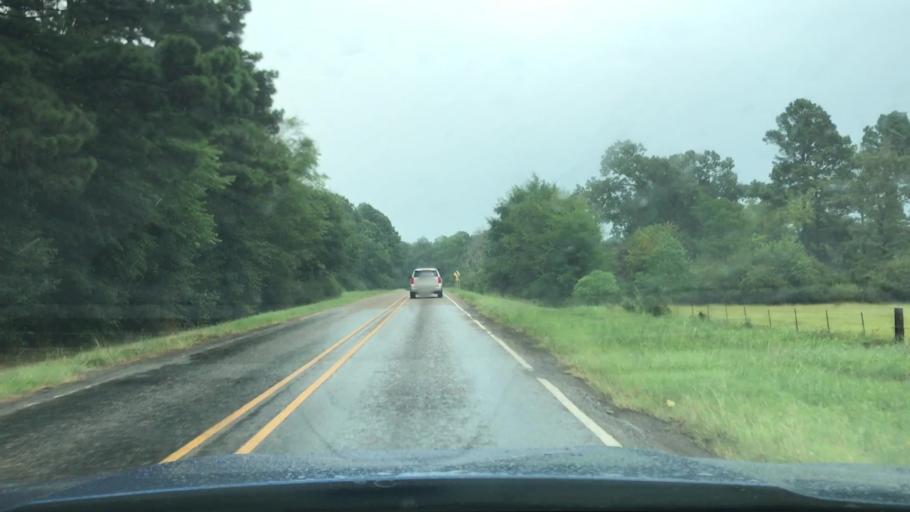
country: US
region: Texas
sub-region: Harrison County
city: Waskom
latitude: 32.4830
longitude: -94.1135
